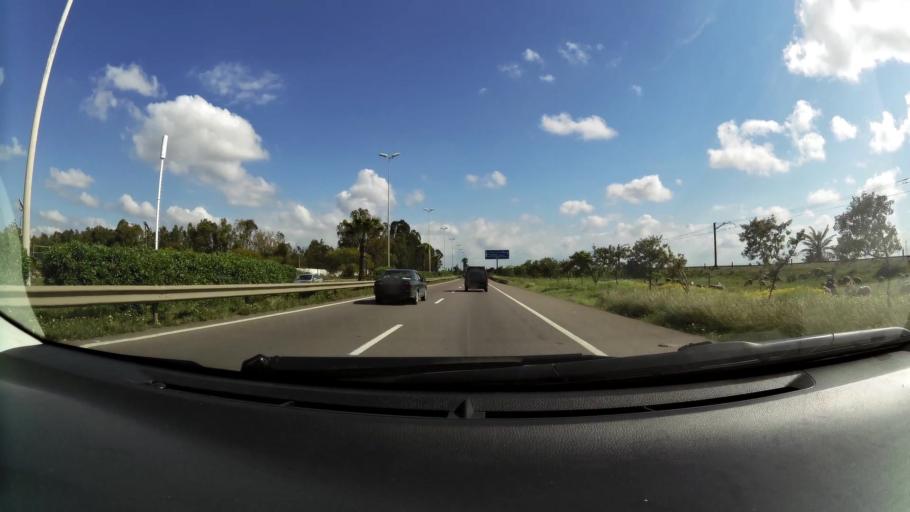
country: MA
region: Chaouia-Ouardigha
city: Nouaseur
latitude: 33.4043
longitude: -7.6235
